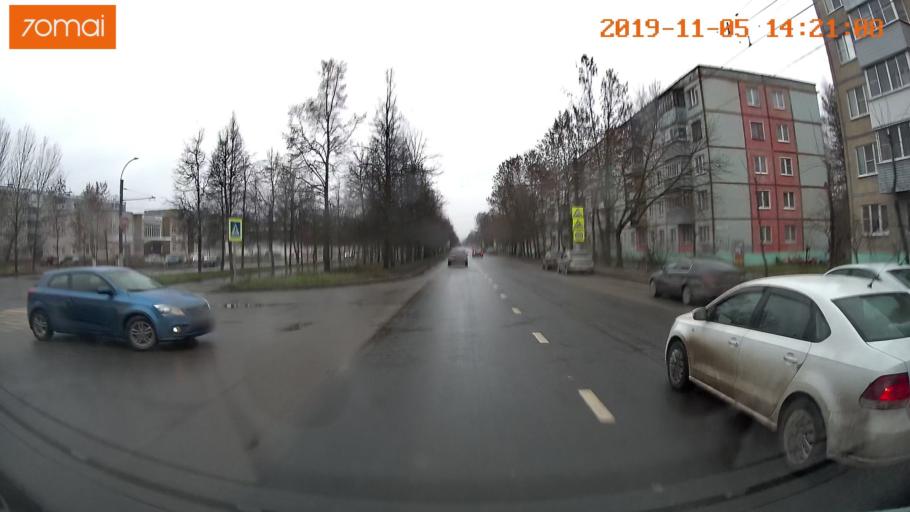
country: RU
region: Ivanovo
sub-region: Gorod Ivanovo
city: Ivanovo
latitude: 56.9573
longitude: 41.0135
